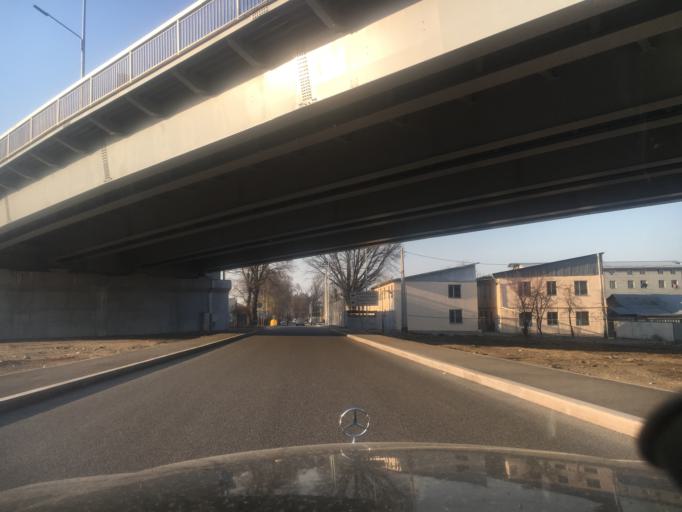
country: KZ
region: Almaty Qalasy
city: Almaty
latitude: 43.2766
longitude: 76.9427
